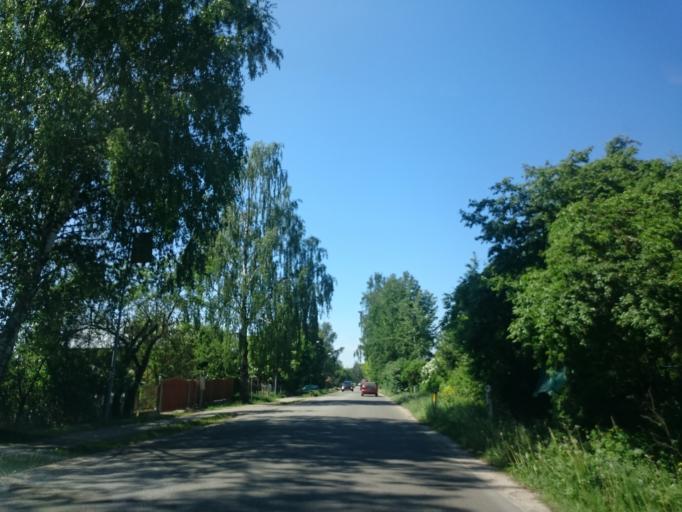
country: LV
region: Marupe
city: Marupe
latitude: 56.8585
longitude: 24.0698
